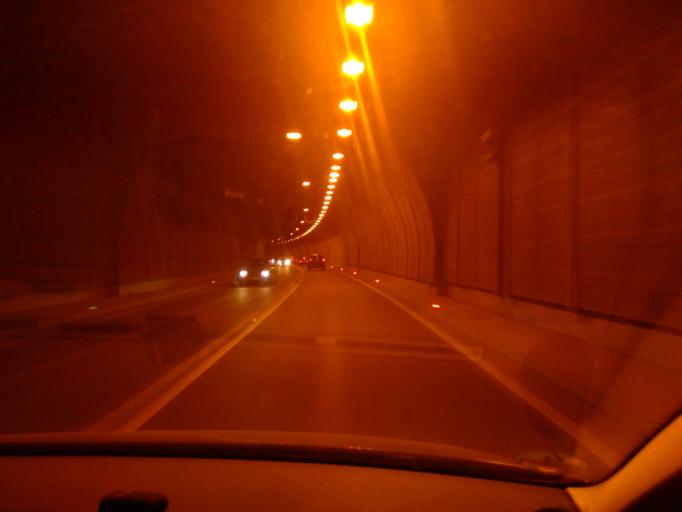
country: AT
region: Salzburg
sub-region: Politischer Bezirk Sankt Johann im Pongau
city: Schwarzach im Pongau
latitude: 47.3166
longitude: 13.1324
